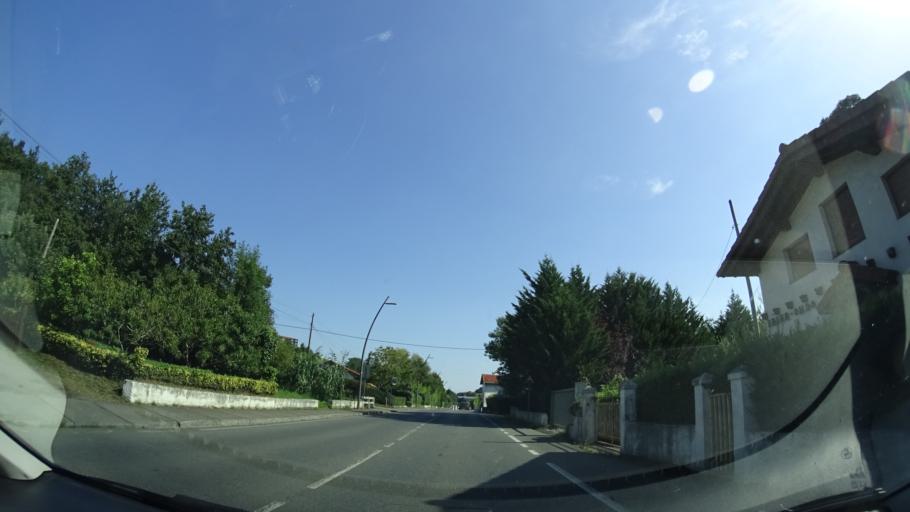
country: ES
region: Basque Country
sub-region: Bizkaia
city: Bakio
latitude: 43.4130
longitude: -2.8138
